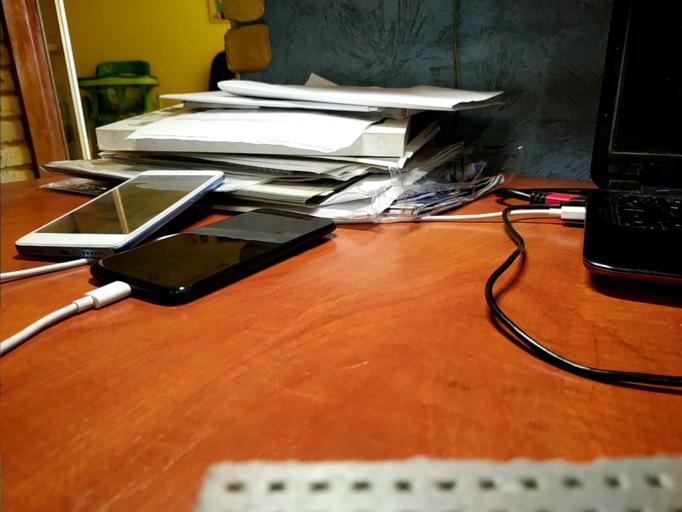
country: RU
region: Tverskaya
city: Kalashnikovo
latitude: 57.4069
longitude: 35.1913
